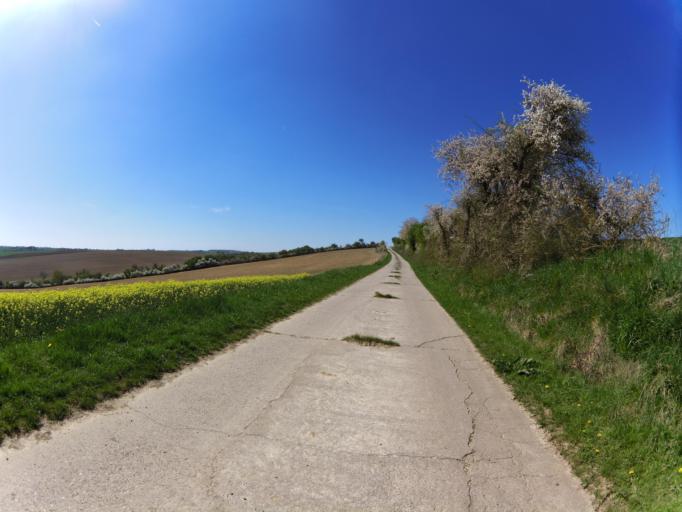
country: DE
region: Bavaria
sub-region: Regierungsbezirk Unterfranken
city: Winterhausen
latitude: 49.6808
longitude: 9.9932
